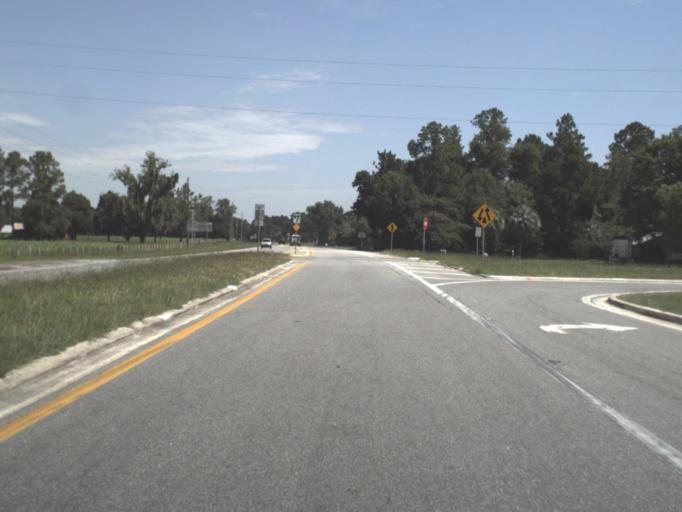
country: US
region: Florida
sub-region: Hamilton County
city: Jasper
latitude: 30.4879
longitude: -82.9301
